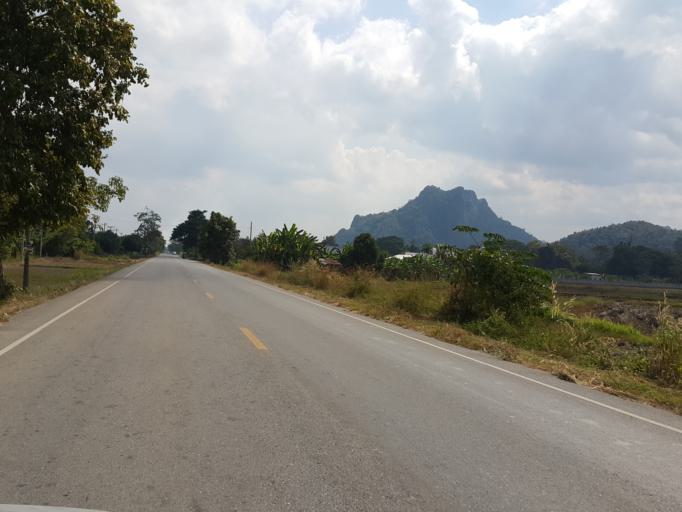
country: TH
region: Sukhothai
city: Thung Saliam
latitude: 17.3329
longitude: 99.4963
